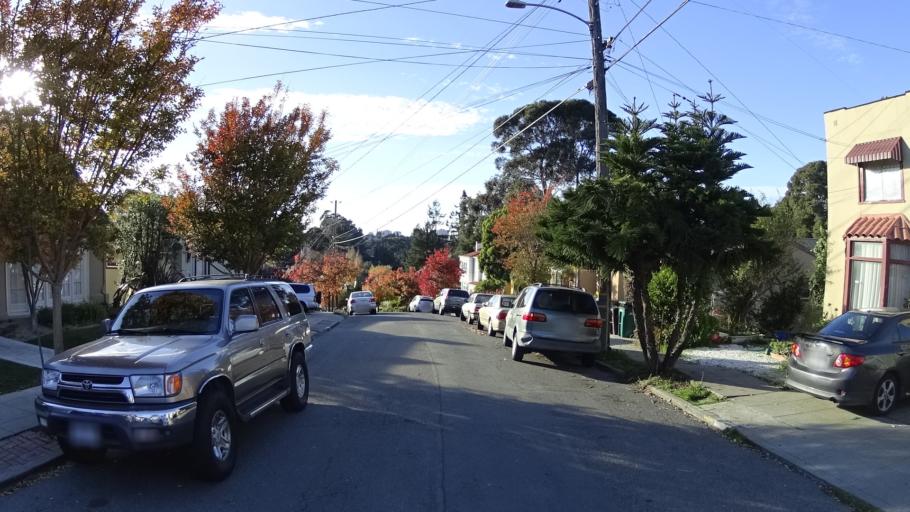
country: US
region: California
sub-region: Alameda County
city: Piedmont
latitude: 37.8070
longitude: -122.2277
